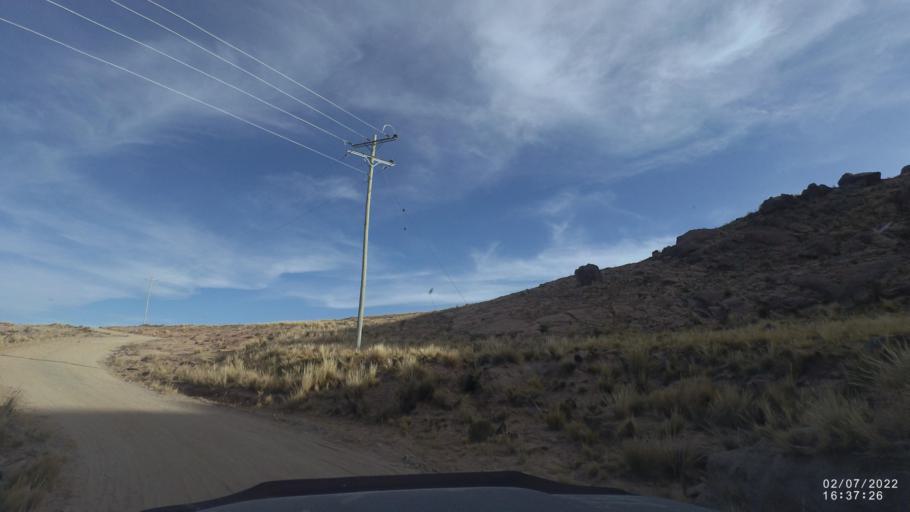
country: BO
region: Cochabamba
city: Irpa Irpa
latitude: -17.9665
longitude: -66.4977
